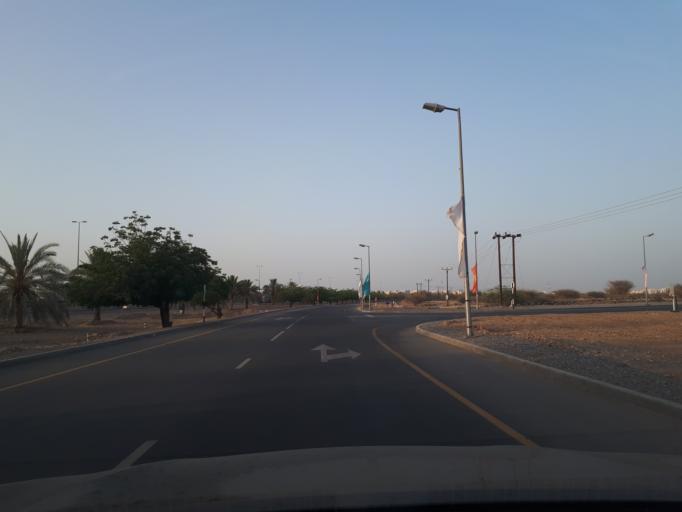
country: OM
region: Muhafazat Masqat
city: As Sib al Jadidah
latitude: 23.5858
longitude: 58.1986
